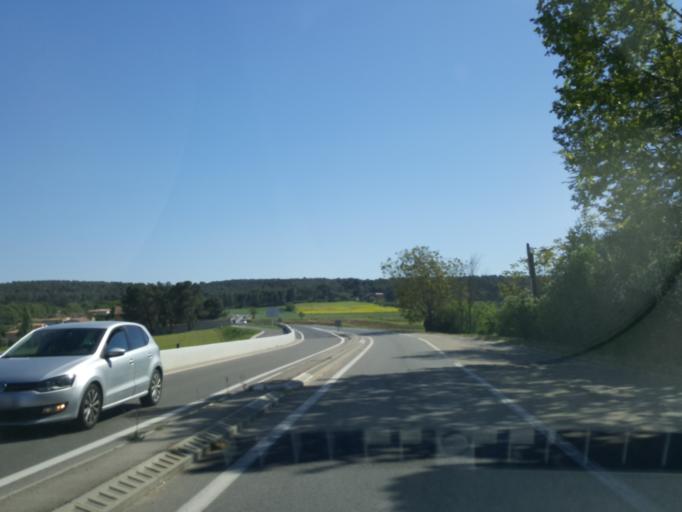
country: FR
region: Provence-Alpes-Cote d'Azur
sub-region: Departement des Bouches-du-Rhone
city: Cabries
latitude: 43.4456
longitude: 5.3606
